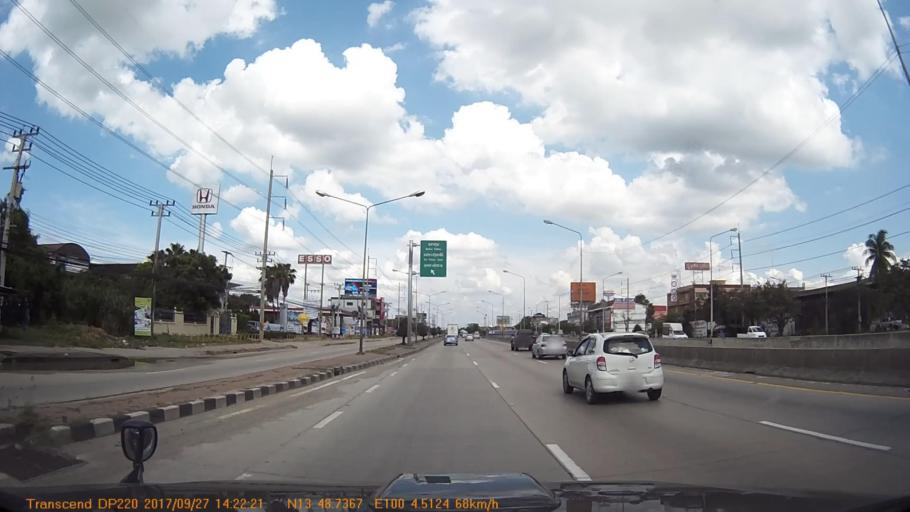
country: TH
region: Nakhon Pathom
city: Nakhon Pathom
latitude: 13.8123
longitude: 100.0753
